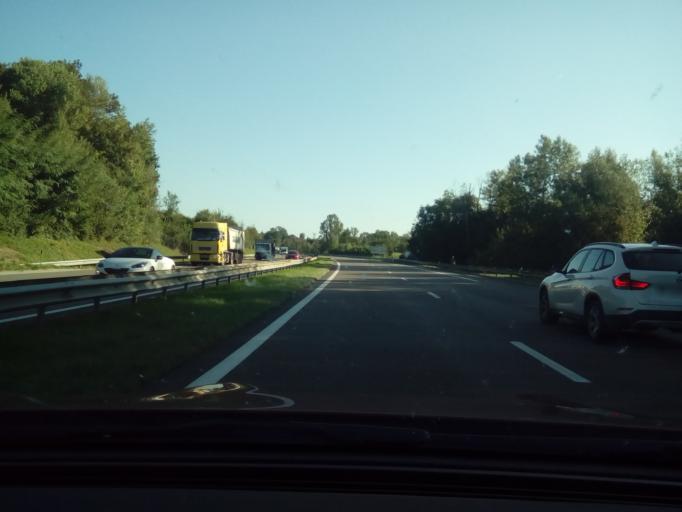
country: FR
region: Rhone-Alpes
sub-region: Departement de la Haute-Savoie
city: Viuz-la-Chiesaz
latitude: 45.8369
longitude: 6.0528
